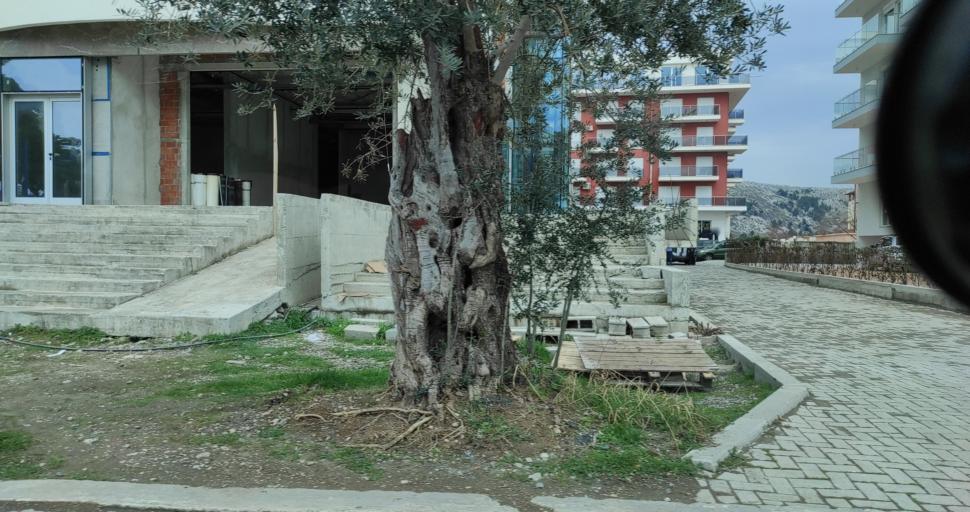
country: AL
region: Lezhe
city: Shengjin
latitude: 41.7998
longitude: 19.6013
